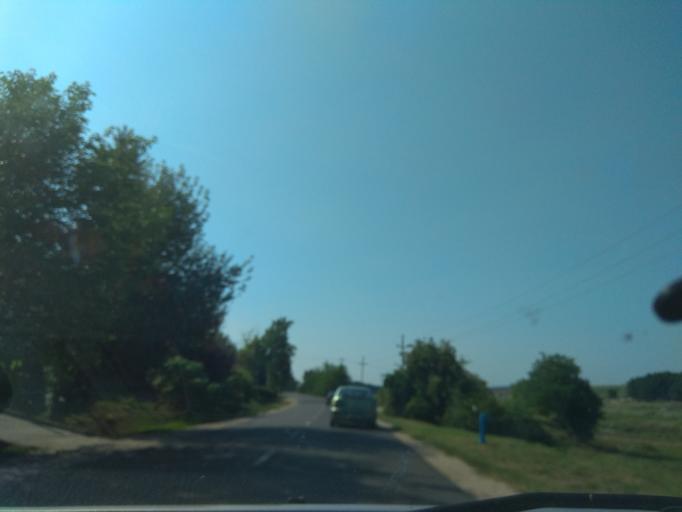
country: HU
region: Borsod-Abauj-Zemplen
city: Harsany
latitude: 47.9574
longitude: 20.7439
